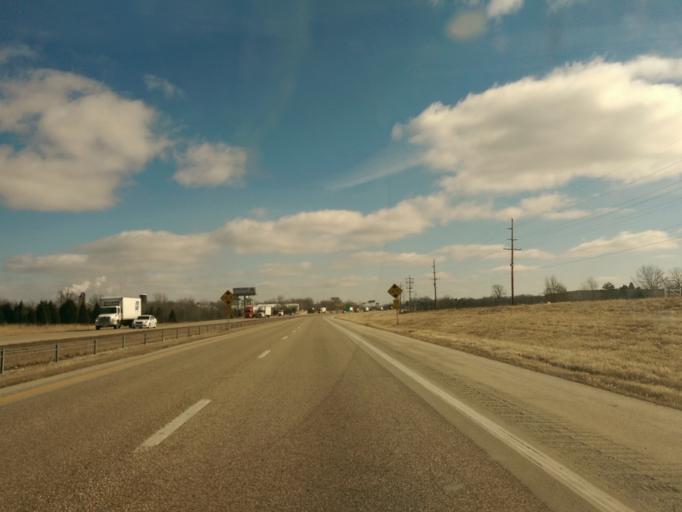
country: US
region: Missouri
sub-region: Montgomery County
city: Montgomery City
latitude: 38.8819
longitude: -91.3955
